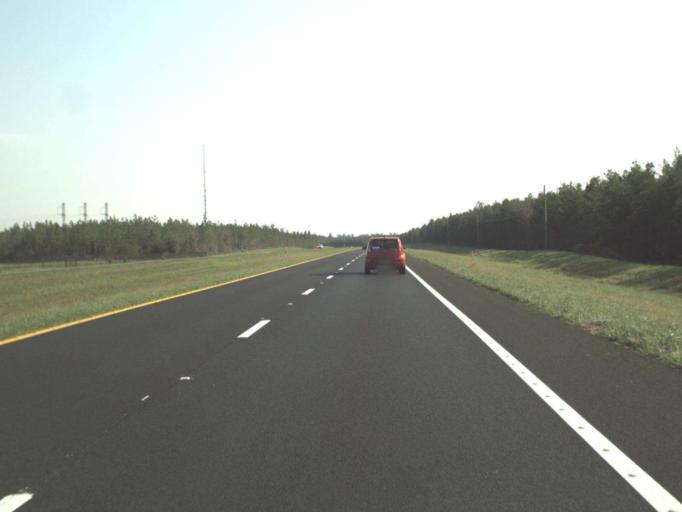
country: US
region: Florida
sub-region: Holmes County
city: Bonifay
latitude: 30.5590
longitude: -85.8147
